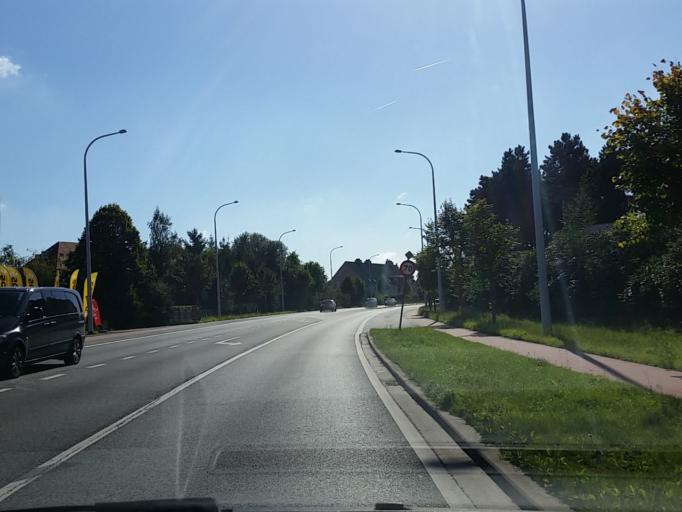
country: BE
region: Flanders
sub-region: Provincie Vlaams-Brabant
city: Herent
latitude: 50.9092
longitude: 4.6773
